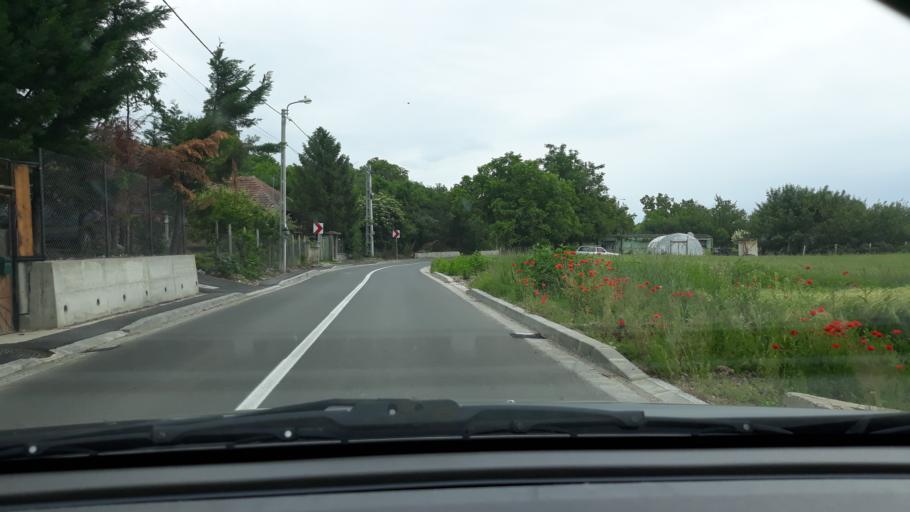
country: RO
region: Bihor
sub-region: Comuna Osorheiu
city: Osorheiu
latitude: 47.0602
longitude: 22.0254
